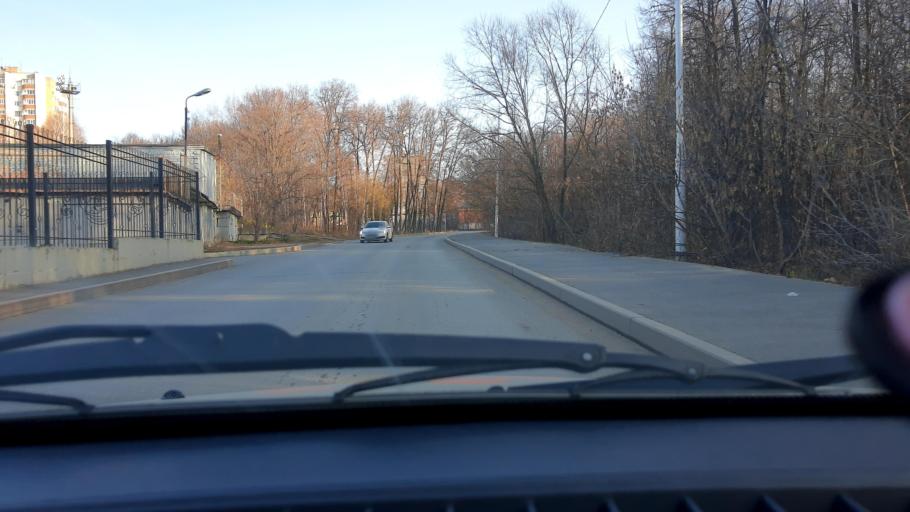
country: RU
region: Bashkortostan
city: Ufa
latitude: 54.7375
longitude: 56.0221
